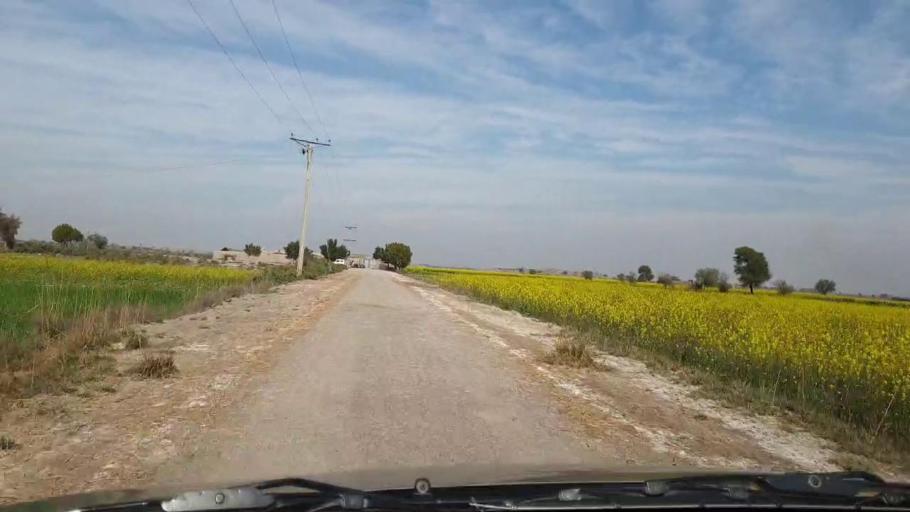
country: PK
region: Sindh
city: Jam Sahib
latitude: 26.2722
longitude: 68.7061
